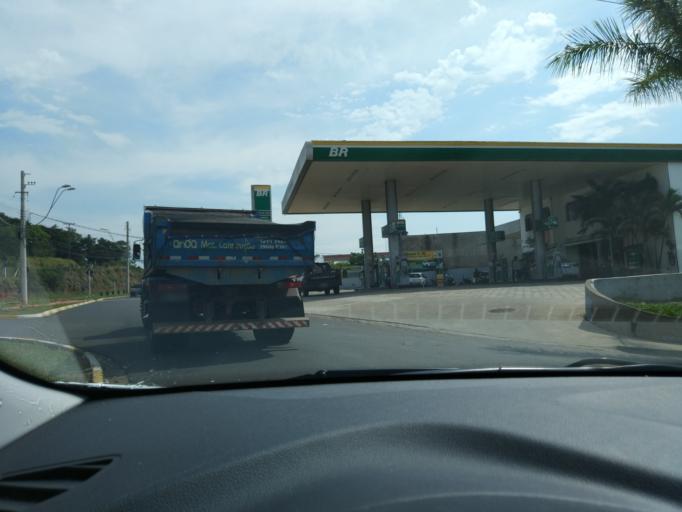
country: BR
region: Sao Paulo
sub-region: Botucatu
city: Botucatu
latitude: -22.8737
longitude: -48.4765
